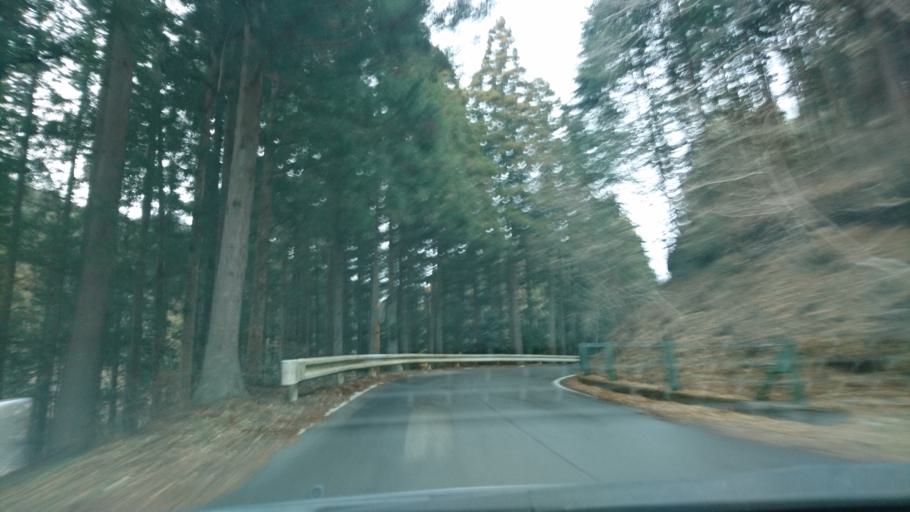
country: JP
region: Iwate
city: Ofunato
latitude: 38.9875
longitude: 141.5528
